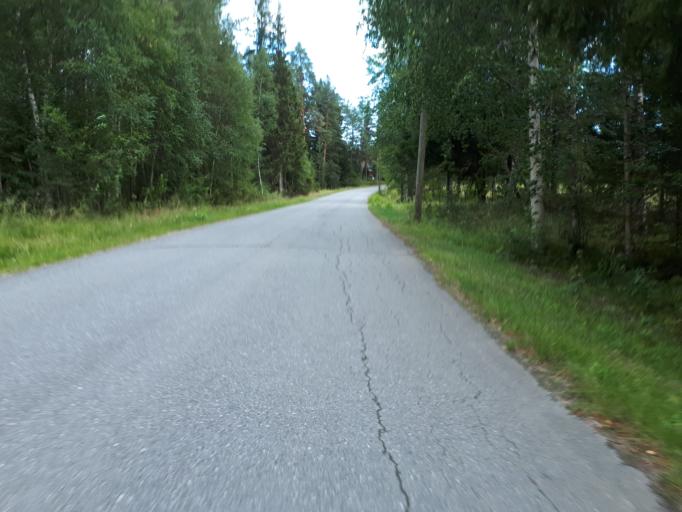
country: FI
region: Northern Ostrobothnia
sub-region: Oulunkaari
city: Ii
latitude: 65.3309
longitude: 25.3957
